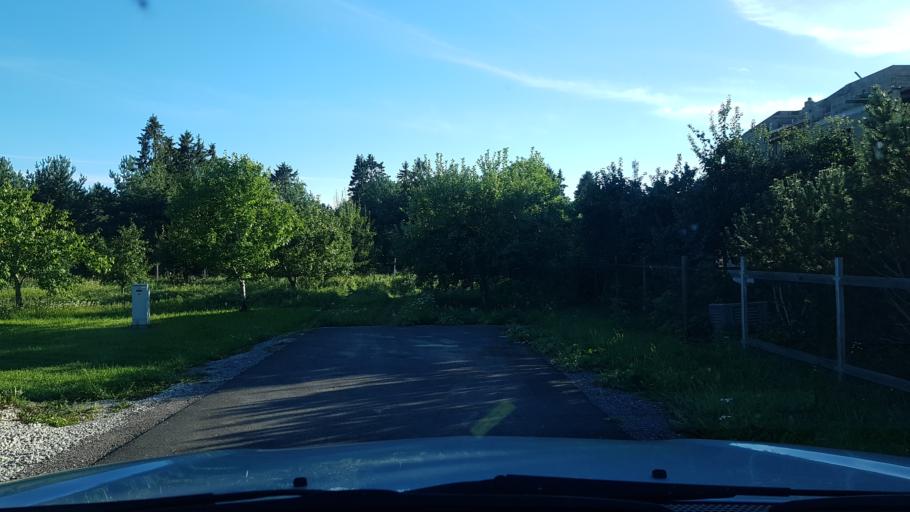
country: EE
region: Harju
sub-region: Rae vald
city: Jueri
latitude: 59.3839
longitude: 24.8462
